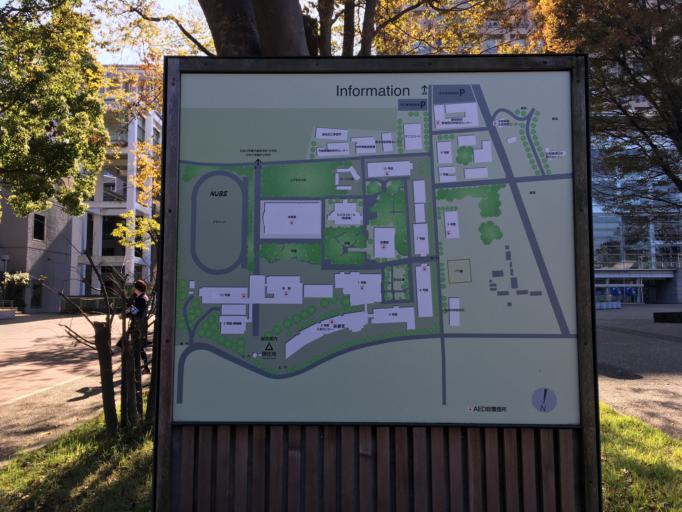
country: JP
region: Kanagawa
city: Fujisawa
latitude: 35.3814
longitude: 139.4700
